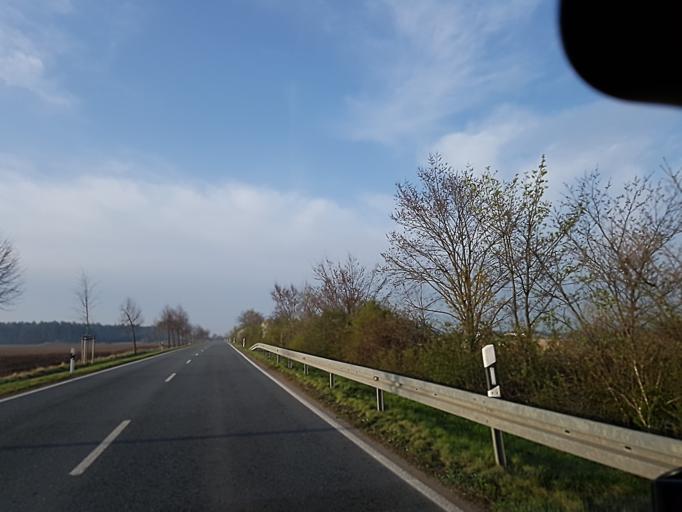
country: DE
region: Saxony
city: Strehla
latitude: 51.3759
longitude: 13.2665
